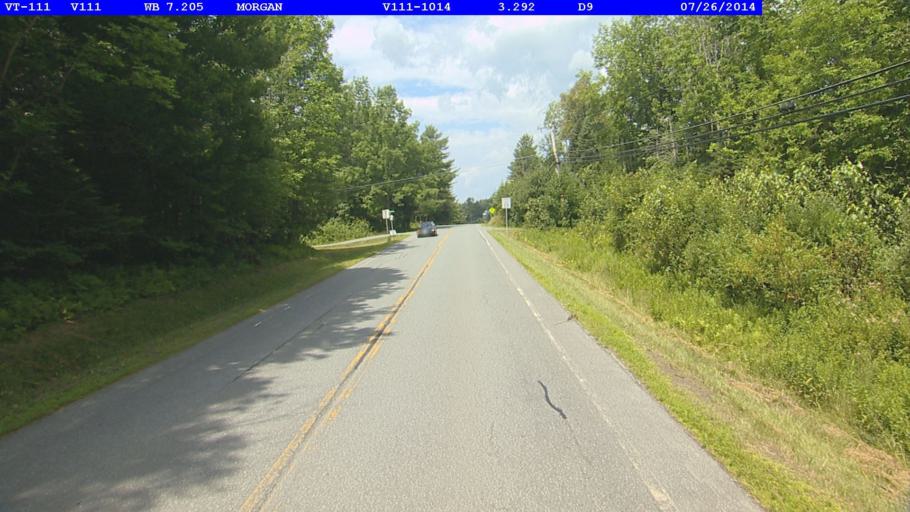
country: US
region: Vermont
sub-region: Orleans County
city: Newport
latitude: 44.9098
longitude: -72.0065
